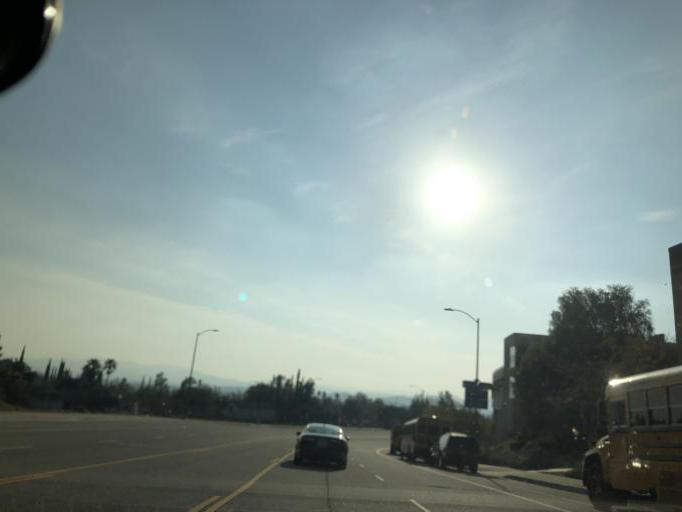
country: US
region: California
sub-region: Los Angeles County
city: Chatsworth
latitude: 34.2714
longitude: -118.5847
